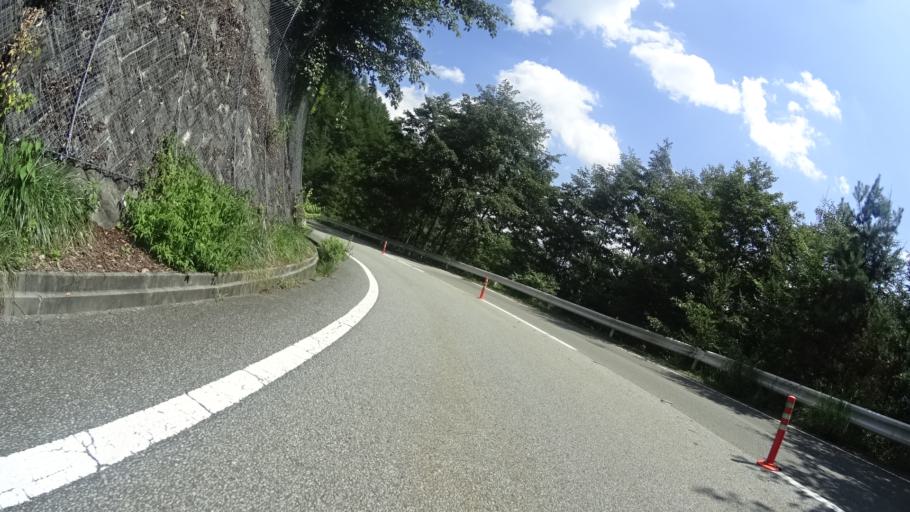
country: JP
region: Yamanashi
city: Enzan
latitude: 35.8008
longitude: 138.6729
